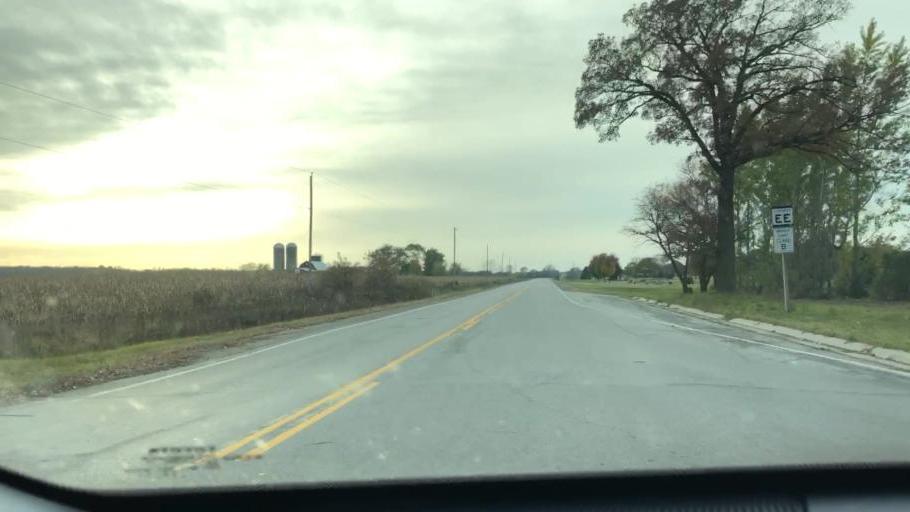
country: US
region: Wisconsin
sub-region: Outagamie County
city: Seymour
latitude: 44.4437
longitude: -88.3315
